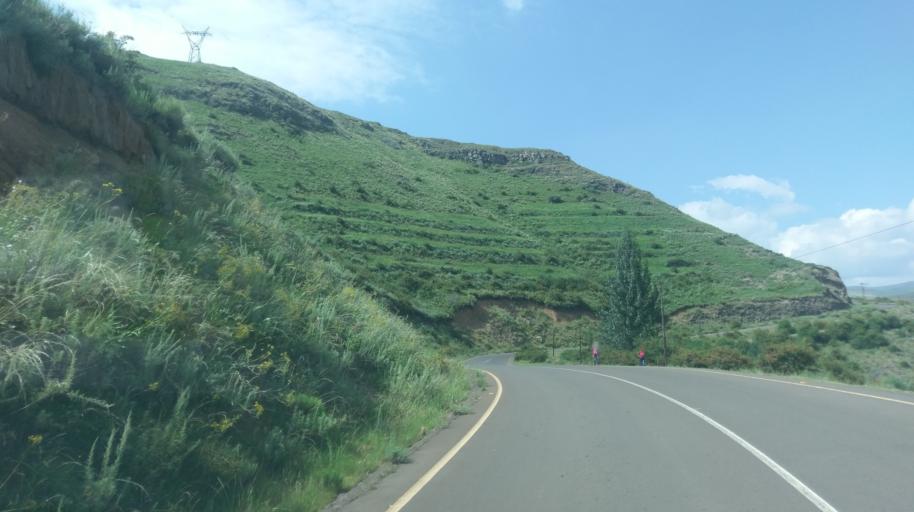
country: LS
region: Thaba-Tseka
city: Thaba-Tseka
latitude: -29.1401
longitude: 28.4906
